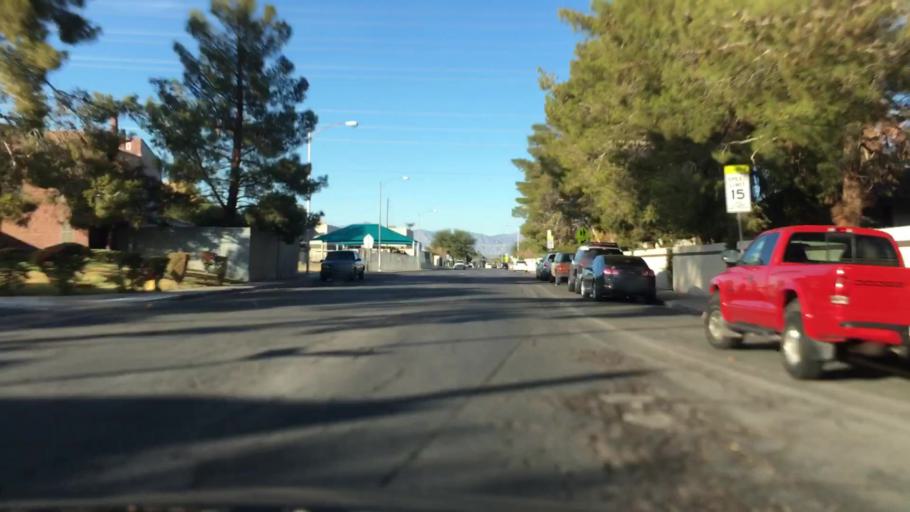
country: US
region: Nevada
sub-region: Clark County
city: Winchester
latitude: 36.1086
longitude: -115.1236
